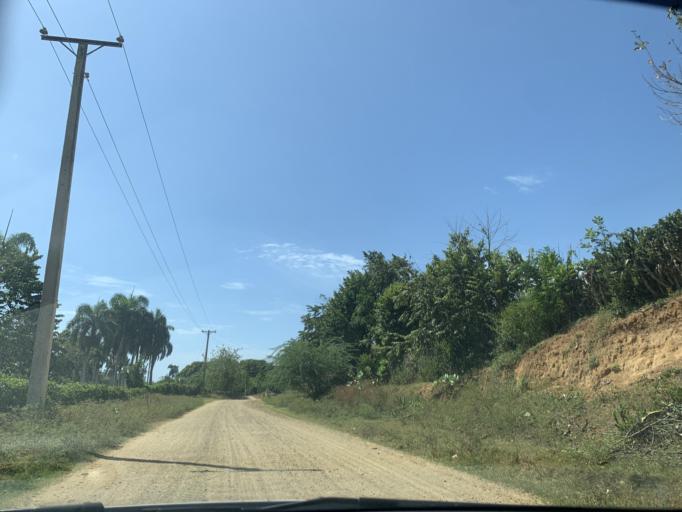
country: DO
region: Puerto Plata
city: Luperon
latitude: 19.8849
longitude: -70.8729
